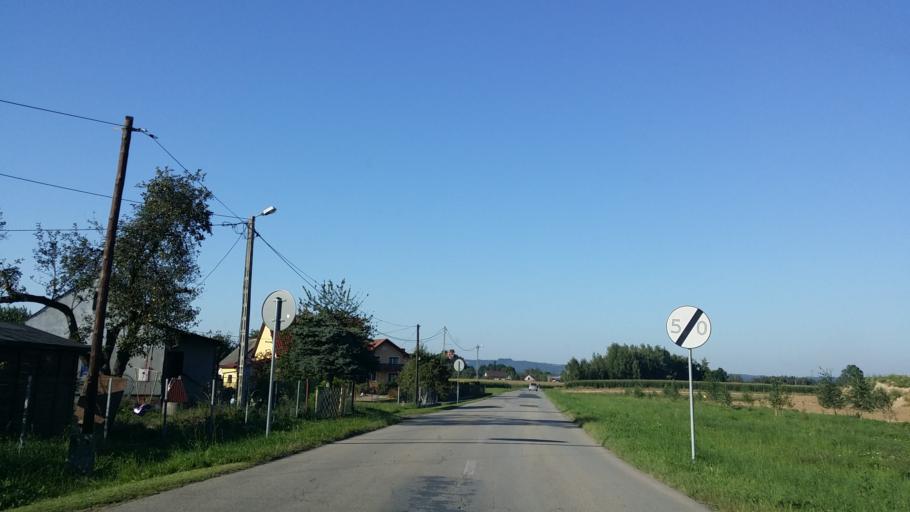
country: PL
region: Lesser Poland Voivodeship
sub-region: Powiat oswiecimski
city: Zator
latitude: 50.0200
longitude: 19.4527
